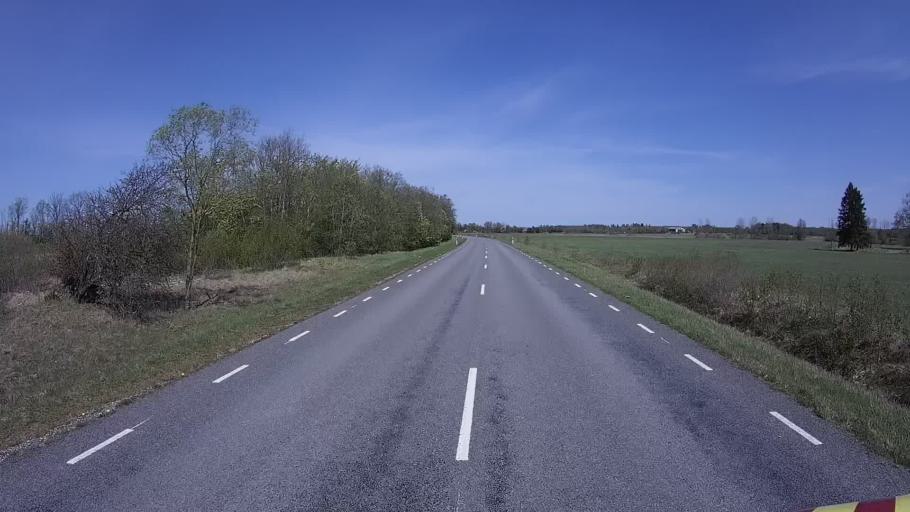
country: EE
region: Laeaene
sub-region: Lihula vald
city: Lihula
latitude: 58.6601
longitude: 23.8363
